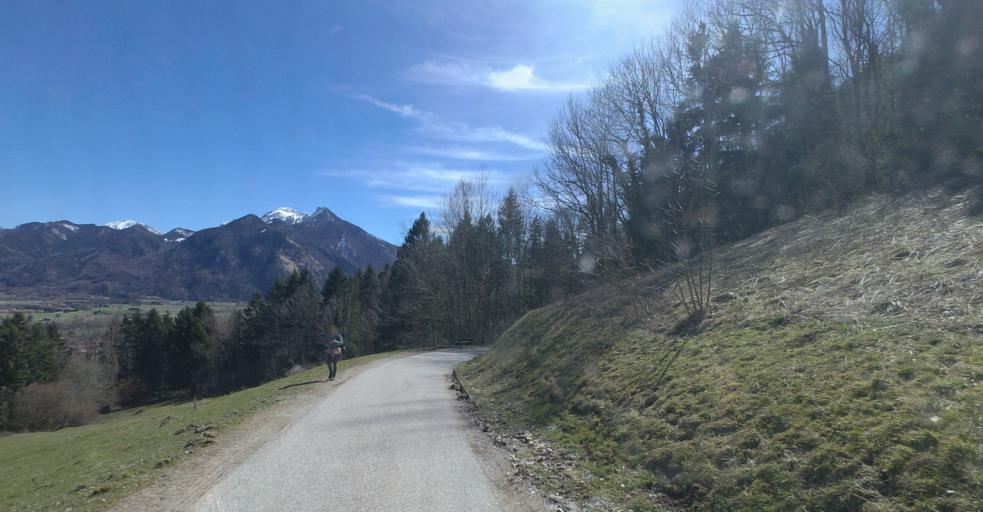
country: DE
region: Bavaria
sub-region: Upper Bavaria
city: Grassau
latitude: 47.7776
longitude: 12.4323
